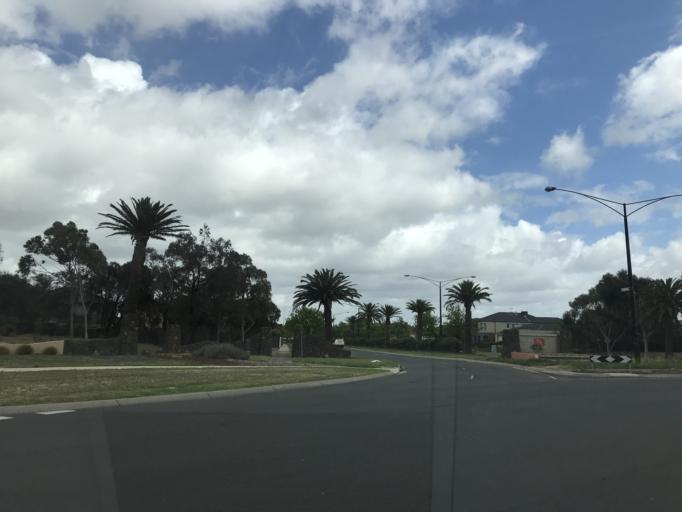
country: AU
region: Victoria
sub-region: Brimbank
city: Derrimut
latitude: -37.7929
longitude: 144.7715
